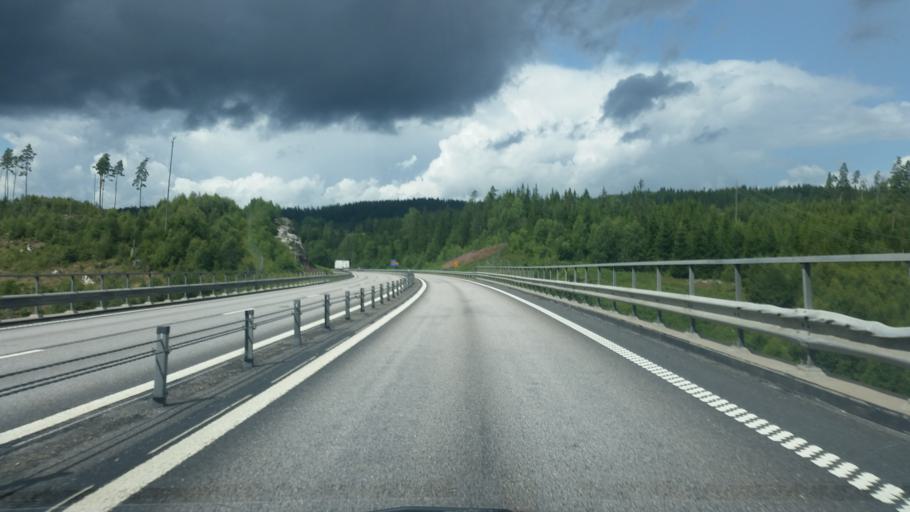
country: SE
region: Vaestra Goetaland
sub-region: Boras Kommun
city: Ganghester
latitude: 57.6689
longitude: 13.0288
